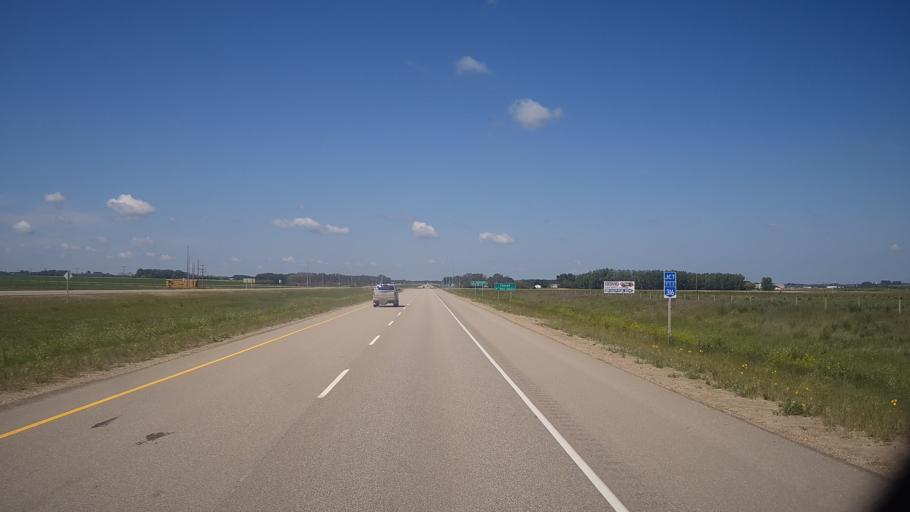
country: CA
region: Saskatchewan
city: Saskatoon
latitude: 52.0123
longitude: -106.3778
